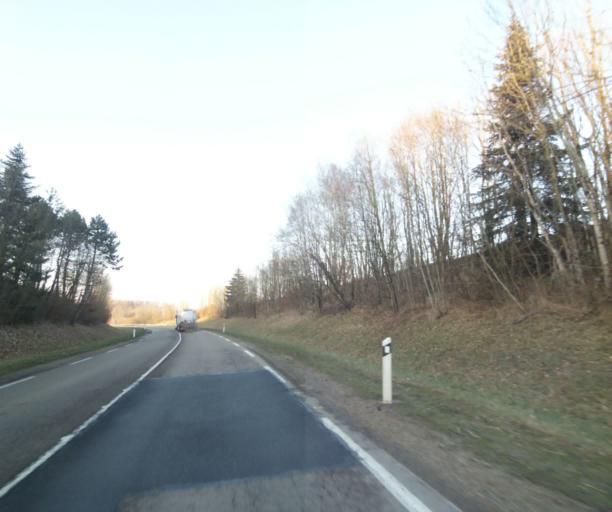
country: FR
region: Champagne-Ardenne
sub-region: Departement de la Haute-Marne
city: Bienville
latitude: 48.5763
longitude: 5.0354
